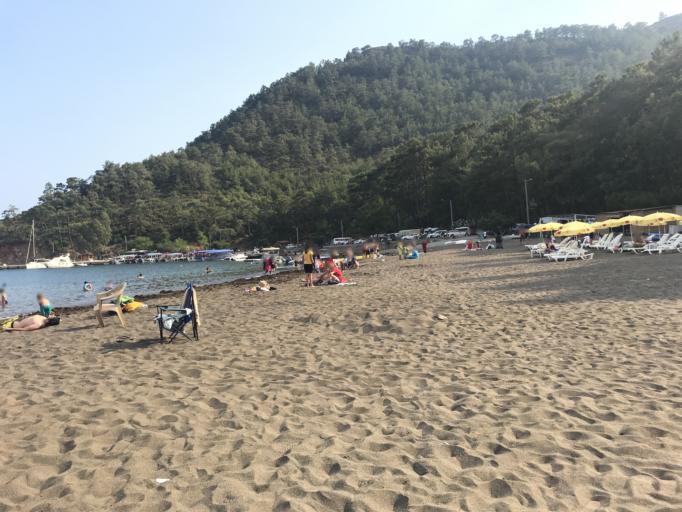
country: TR
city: Dalyan
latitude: 36.8302
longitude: 28.5489
